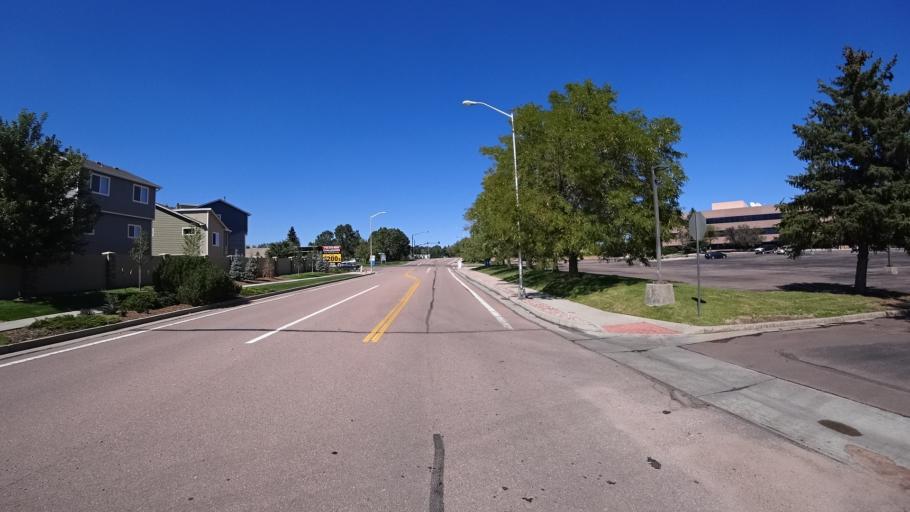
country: US
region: Colorado
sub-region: El Paso County
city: Cimarron Hills
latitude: 38.8449
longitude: -104.7228
